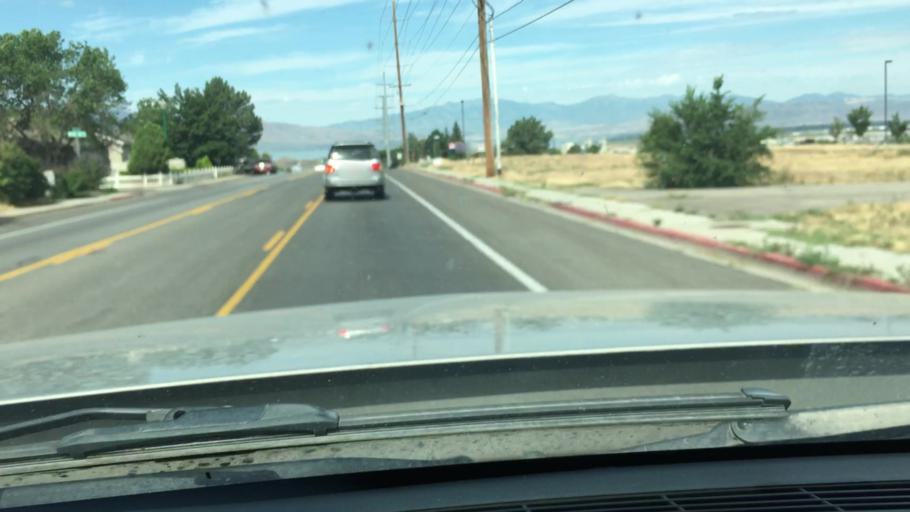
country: US
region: Utah
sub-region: Utah County
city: Lindon
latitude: 40.3264
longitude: -111.7220
